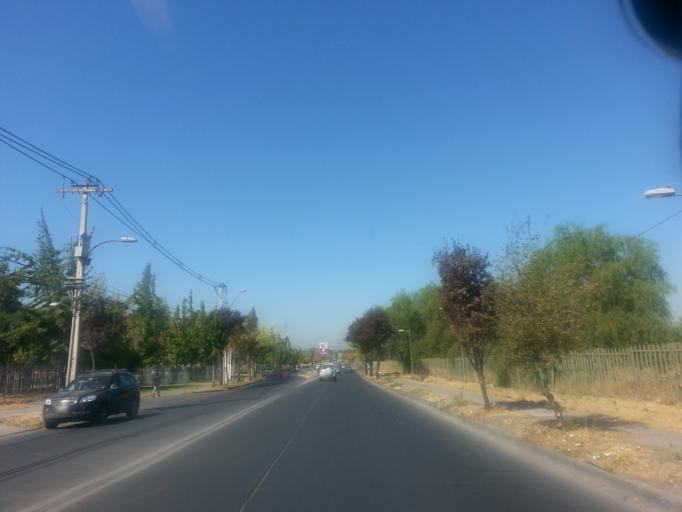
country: CL
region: Santiago Metropolitan
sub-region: Provincia de Santiago
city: Villa Presidente Frei, Nunoa, Santiago, Chile
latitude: -33.4588
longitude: -70.5463
